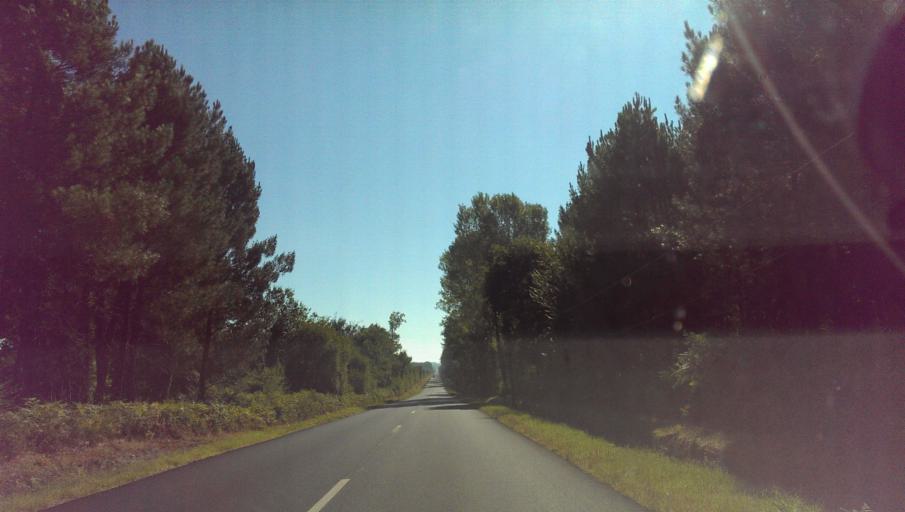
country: FR
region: Aquitaine
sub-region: Departement du Lot-et-Garonne
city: Casteljaloux
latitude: 44.2028
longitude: 0.0966
